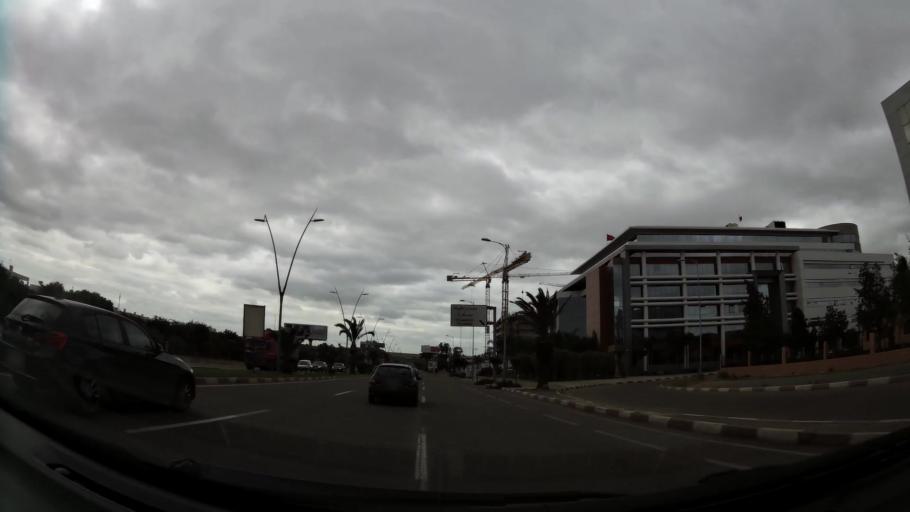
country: MA
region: Grand Casablanca
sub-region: Casablanca
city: Casablanca
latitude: 33.5223
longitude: -7.6346
